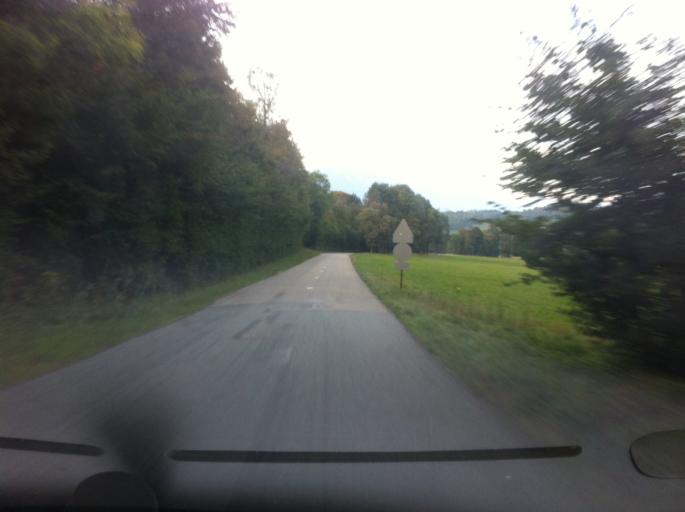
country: FR
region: Rhone-Alpes
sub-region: Departement de la Savoie
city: Mercury
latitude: 45.6928
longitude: 6.3079
